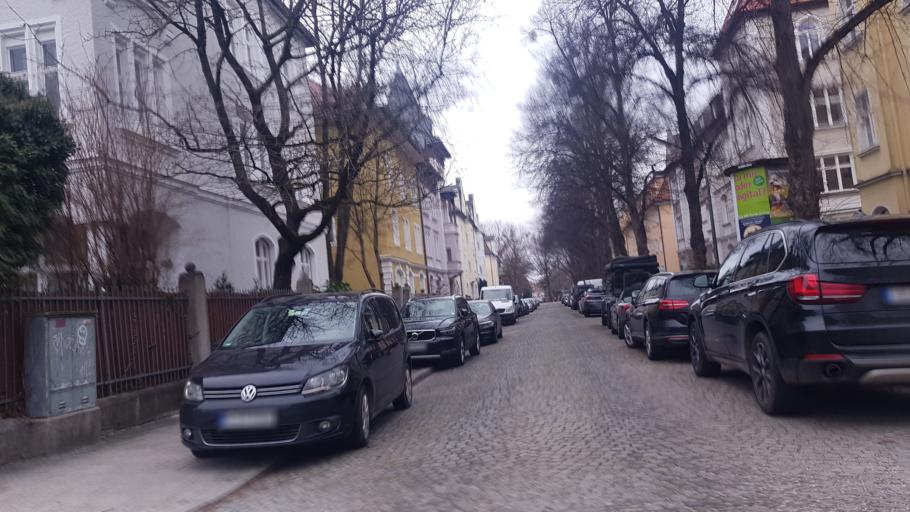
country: DE
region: Bavaria
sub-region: Upper Bavaria
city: Munich
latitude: 48.1570
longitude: 11.5167
